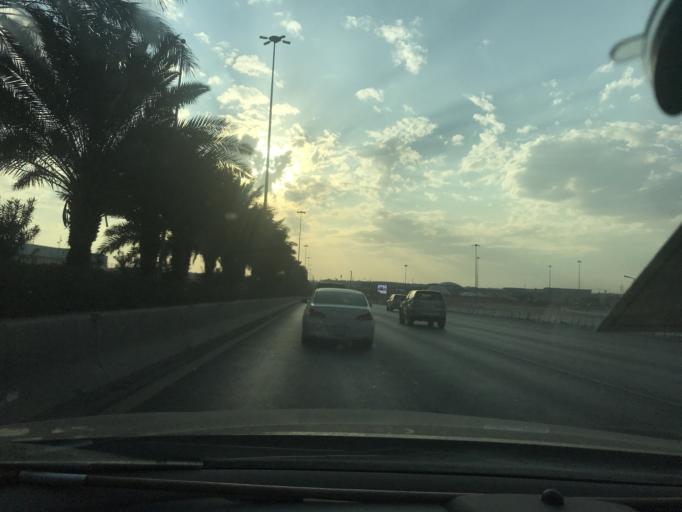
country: SA
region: Ar Riyad
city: Riyadh
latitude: 24.7585
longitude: 46.6407
